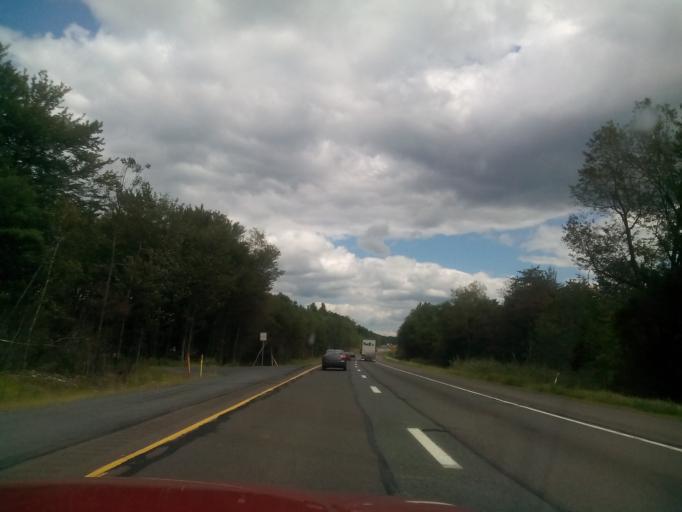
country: US
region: Pennsylvania
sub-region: Carbon County
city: Indian Mountain Lake
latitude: 41.0780
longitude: -75.5261
